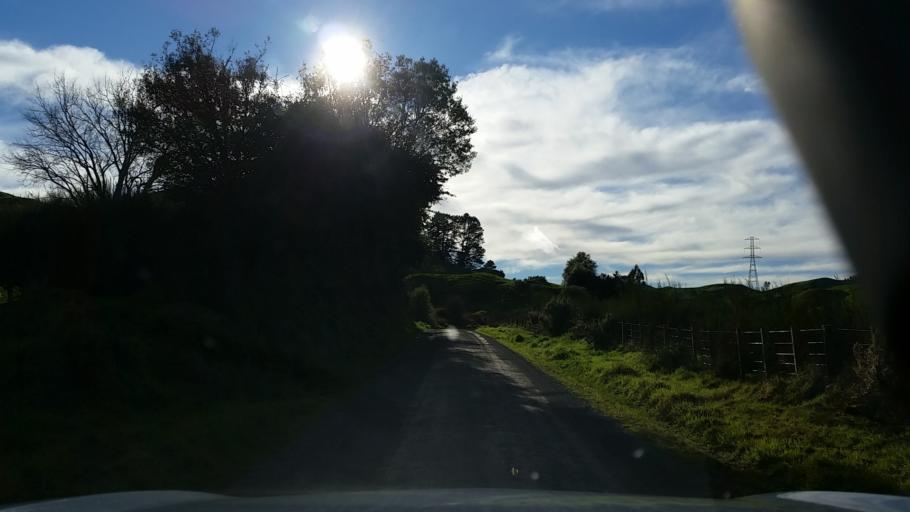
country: NZ
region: Waikato
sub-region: South Waikato District
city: Tokoroa
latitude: -38.3639
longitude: 176.0896
